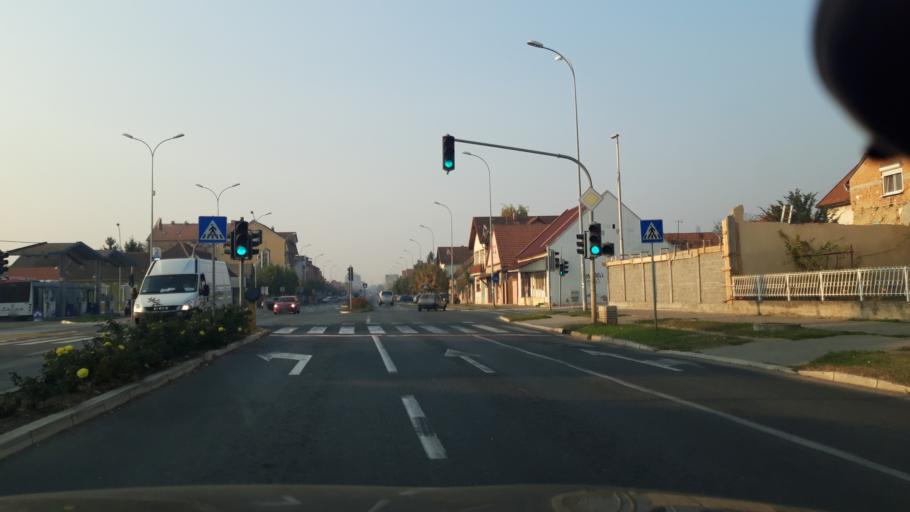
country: RS
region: Autonomna Pokrajina Vojvodina
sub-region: Sremski Okrug
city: Ingija
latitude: 45.0408
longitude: 20.0882
